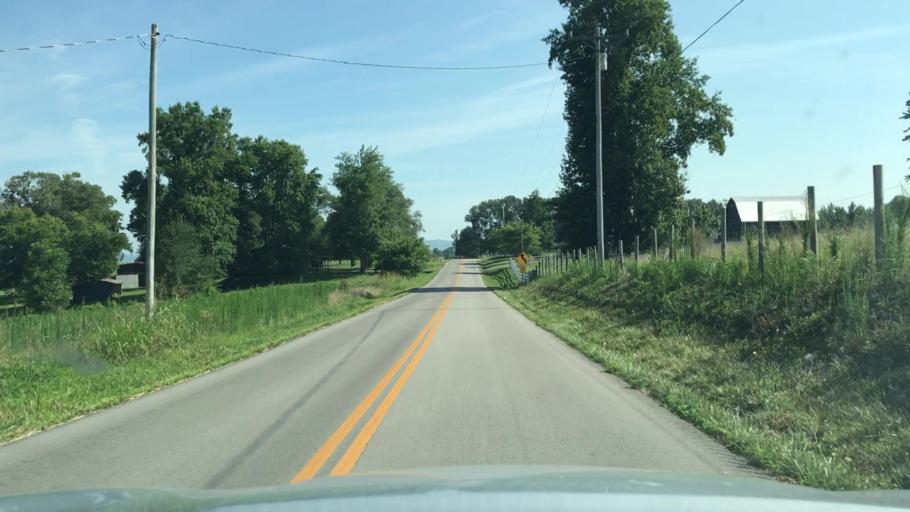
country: US
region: Tennessee
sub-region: Pickett County
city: Byrdstown
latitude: 36.6244
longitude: -85.0846
